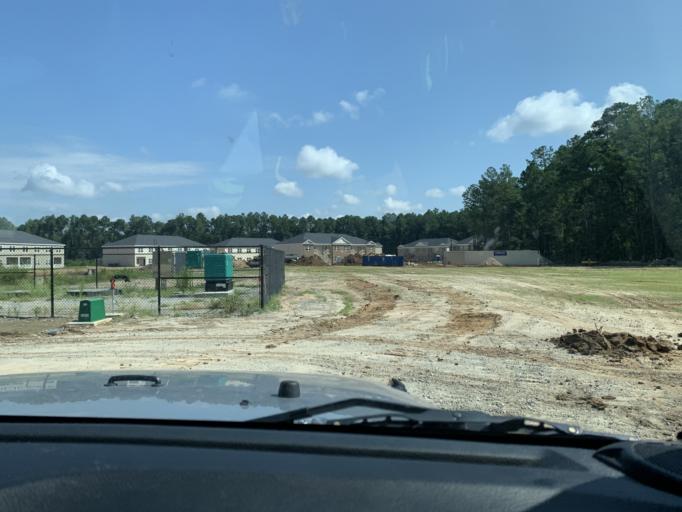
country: US
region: Georgia
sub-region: Chatham County
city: Bloomingdale
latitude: 32.1337
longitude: -81.2902
